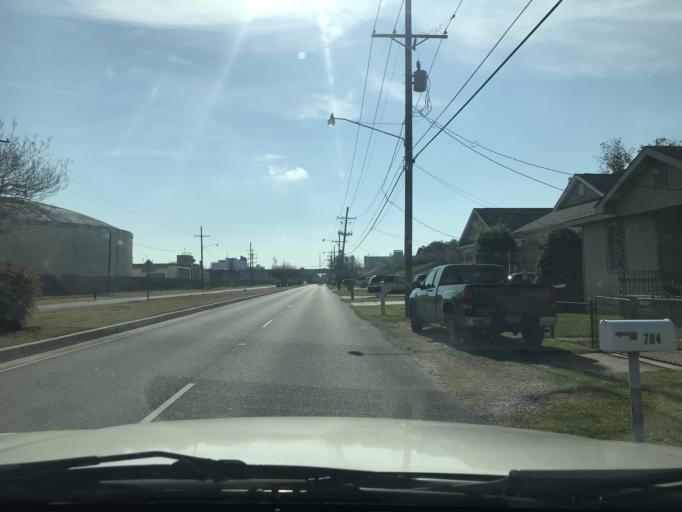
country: US
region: Louisiana
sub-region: Jefferson Parish
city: Marrero
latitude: 29.8987
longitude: -90.0967
